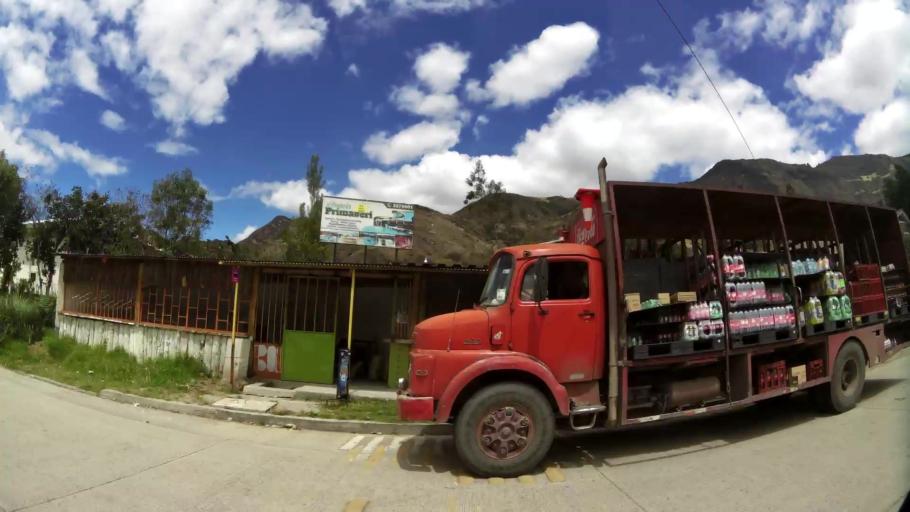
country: EC
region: Azuay
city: Cuenca
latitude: -3.1348
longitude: -79.1328
